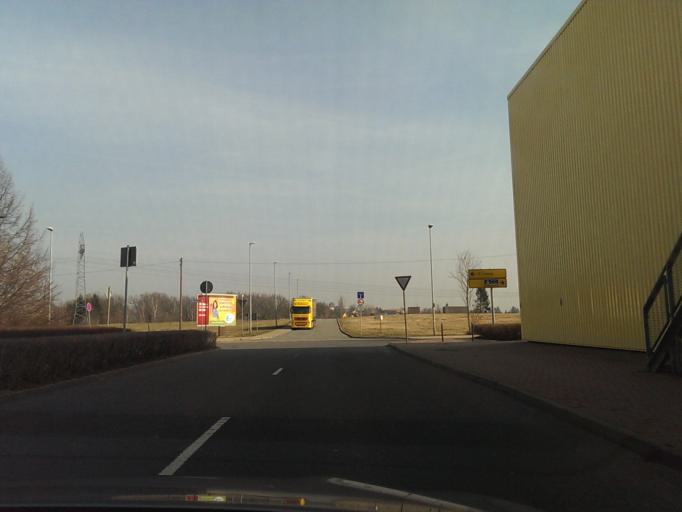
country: DE
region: Saxony
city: Wittgensdorf
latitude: 50.8670
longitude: 12.8634
